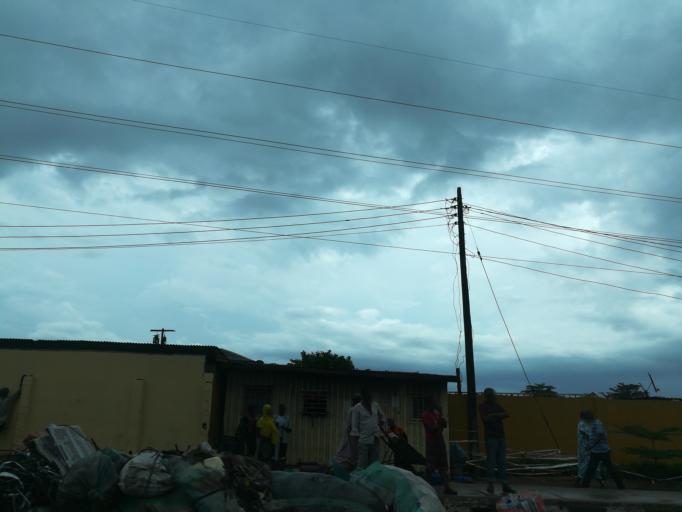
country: NG
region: Lagos
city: Ojota
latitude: 6.6103
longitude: 3.4113
